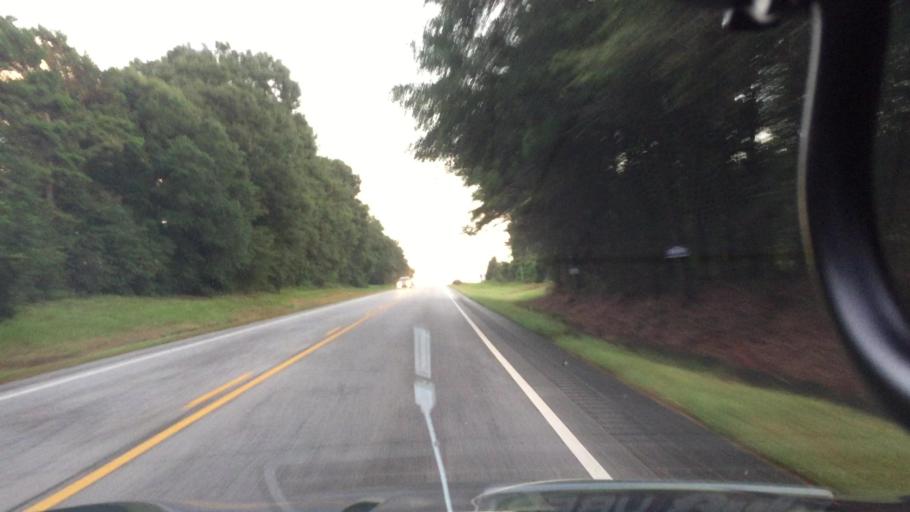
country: US
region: Alabama
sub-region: Coffee County
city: New Brockton
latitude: 31.4339
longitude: -85.8905
